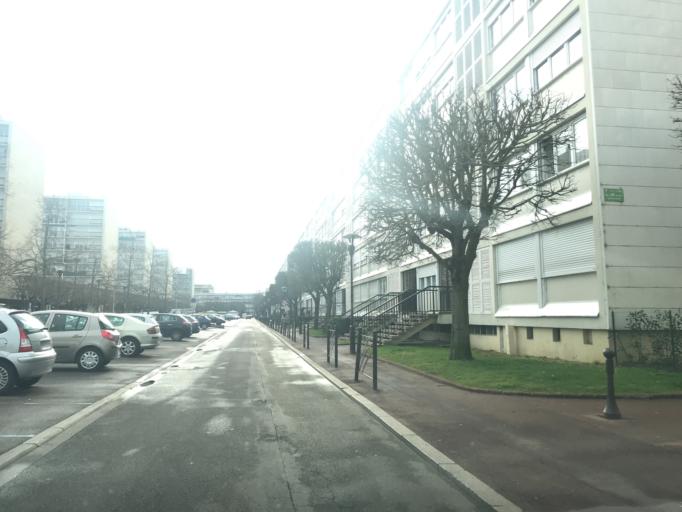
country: FR
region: Ile-de-France
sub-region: Departement des Yvelines
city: Velizy-Villacoublay
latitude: 48.7841
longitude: 2.1816
